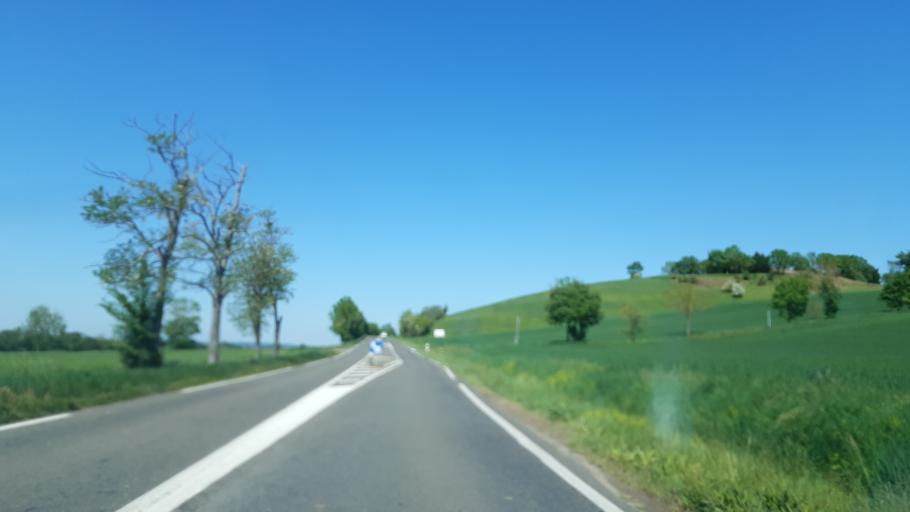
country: FR
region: Midi-Pyrenees
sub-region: Departement du Gers
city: Pujaudran
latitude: 43.5888
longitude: 1.0529
